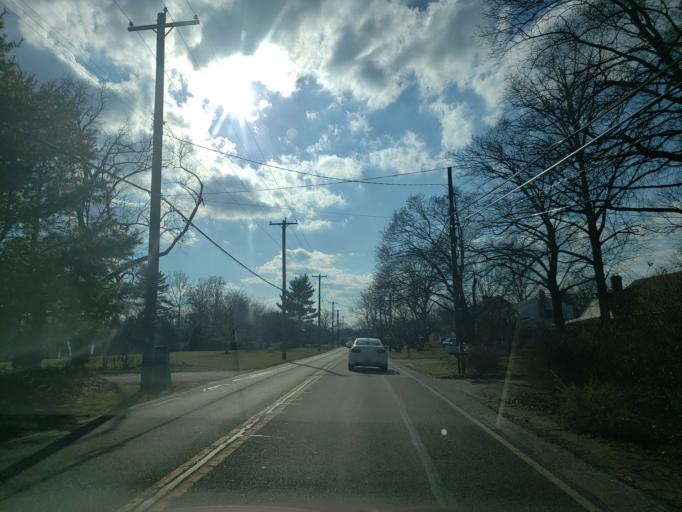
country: US
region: Pennsylvania
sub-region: Montgomery County
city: Norristown
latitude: 40.1423
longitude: -75.3240
